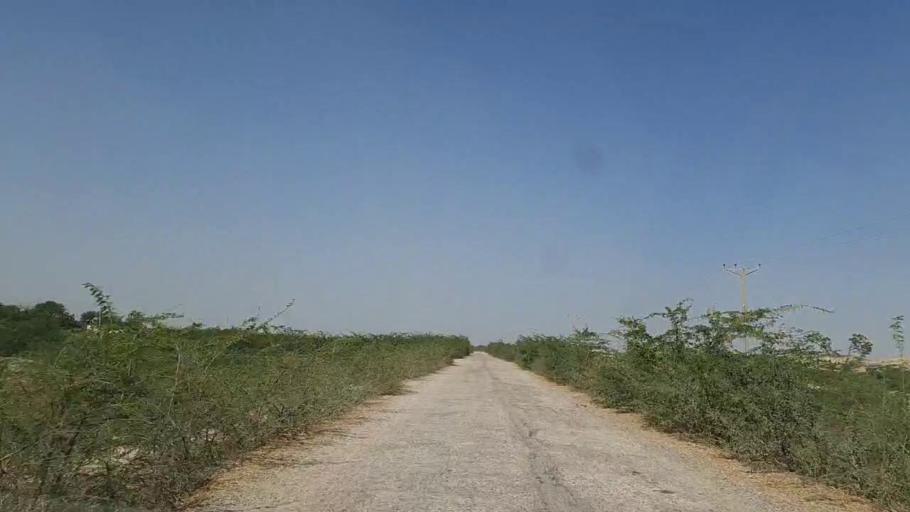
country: PK
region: Sindh
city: Naukot
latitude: 24.6336
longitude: 69.2882
